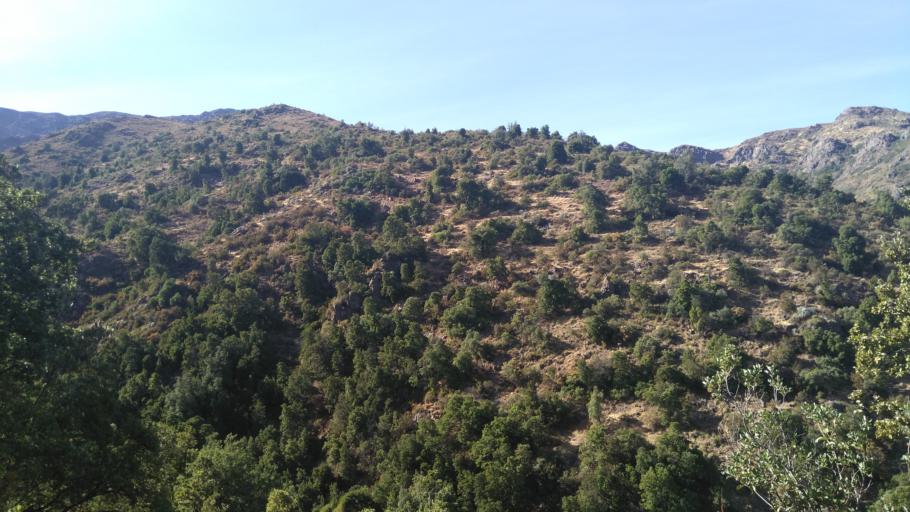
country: CL
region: Santiago Metropolitan
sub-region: Provincia de Cordillera
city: Puente Alto
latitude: -33.7100
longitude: -70.4551
